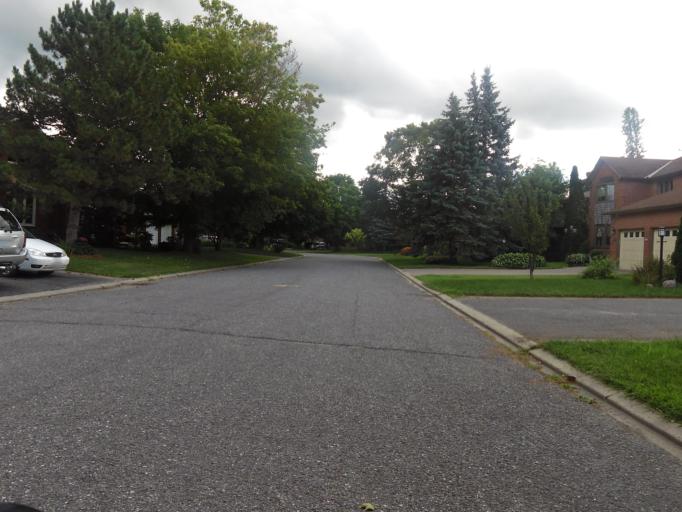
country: CA
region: Ontario
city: Bells Corners
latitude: 45.3234
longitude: -75.9105
